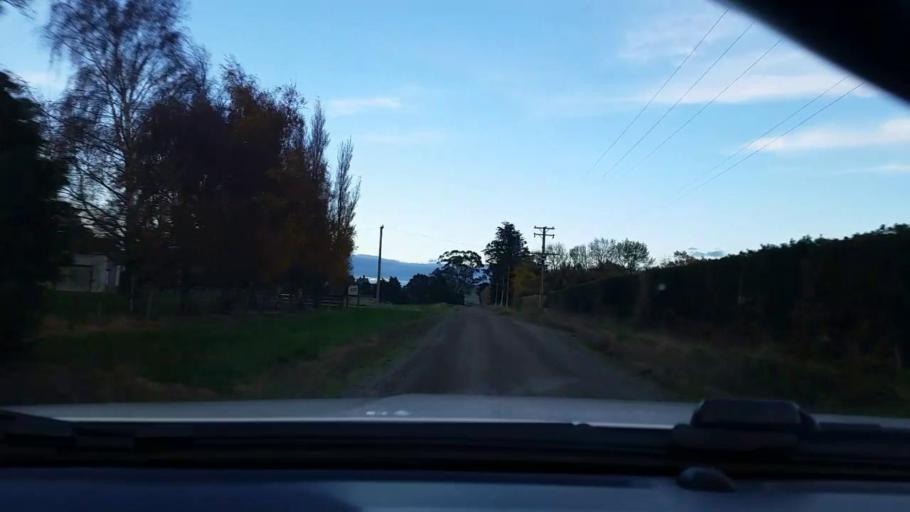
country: NZ
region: Southland
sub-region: Southland District
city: Winton
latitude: -46.1035
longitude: 168.4617
